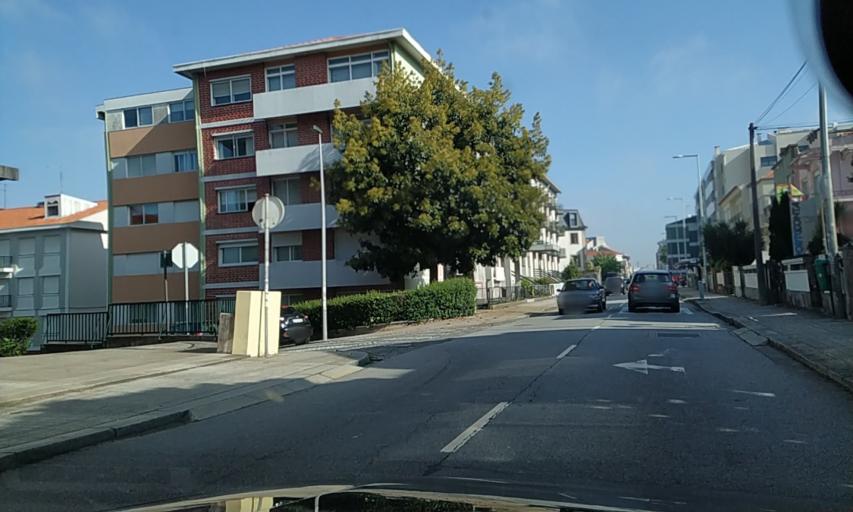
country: PT
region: Porto
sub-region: Porto
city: Porto
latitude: 41.1617
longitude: -8.6247
